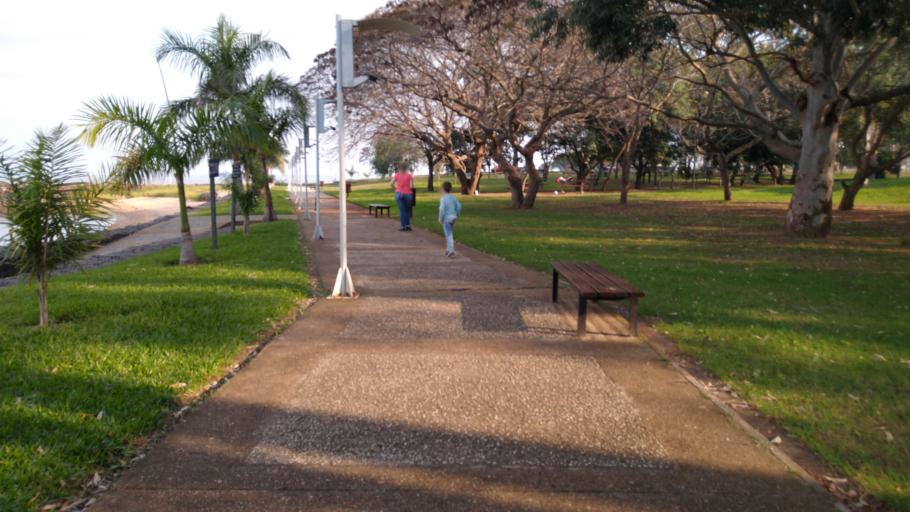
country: AR
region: Entre Rios
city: Santa Ana
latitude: -30.9132
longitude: -57.9251
